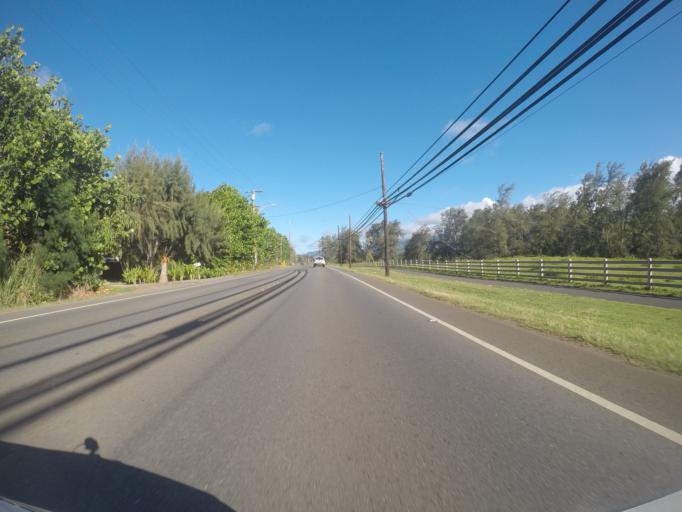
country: US
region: Hawaii
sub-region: Honolulu County
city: Kahuku
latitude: 21.6646
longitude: -157.9364
